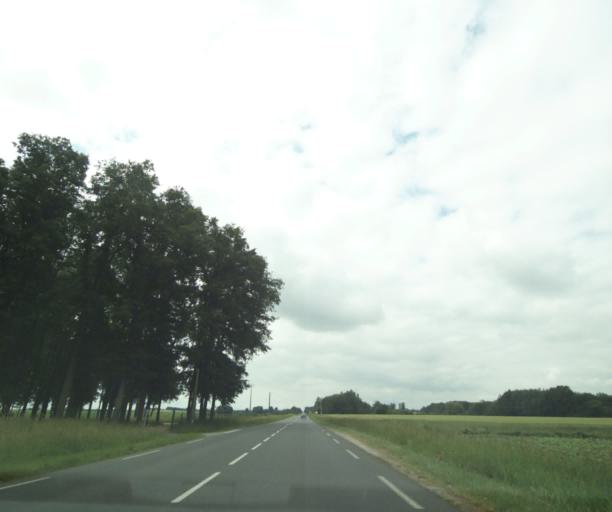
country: FR
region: Pays de la Loire
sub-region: Departement de Maine-et-Loire
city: Distre
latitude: 47.1825
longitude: -0.1324
